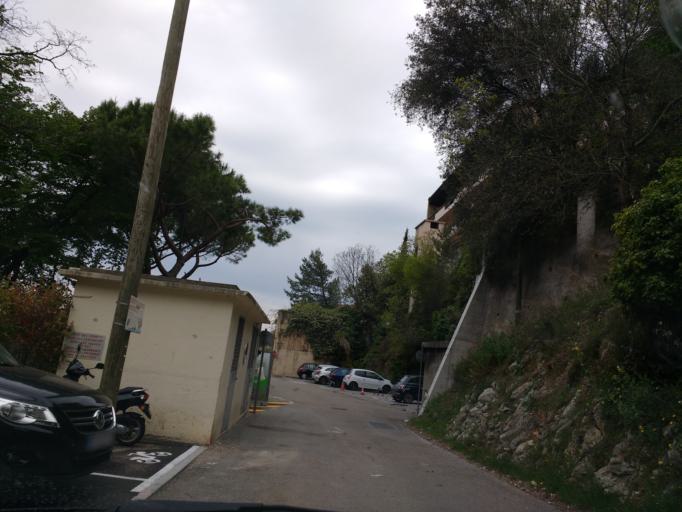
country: FR
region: Provence-Alpes-Cote d'Azur
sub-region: Departement des Alpes-Maritimes
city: Eze
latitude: 43.7318
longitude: 7.3642
